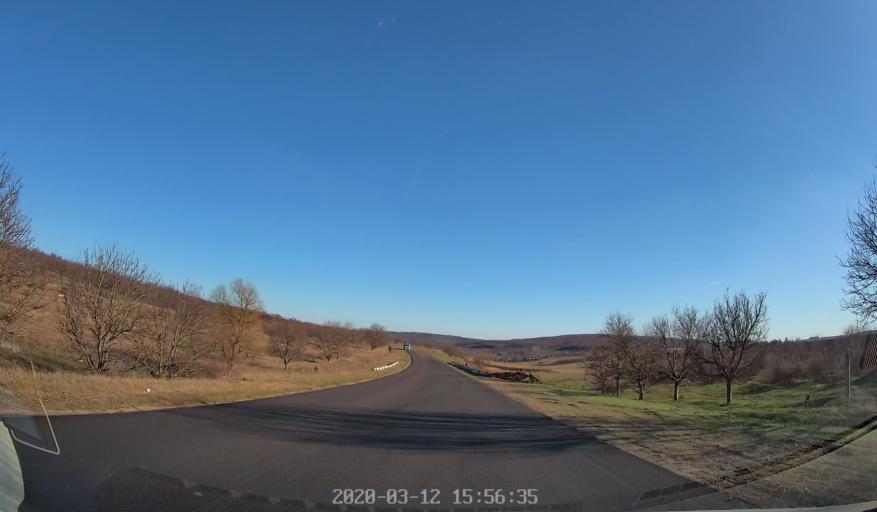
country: MD
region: Chisinau
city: Vadul lui Voda
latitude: 47.0619
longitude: 29.0338
